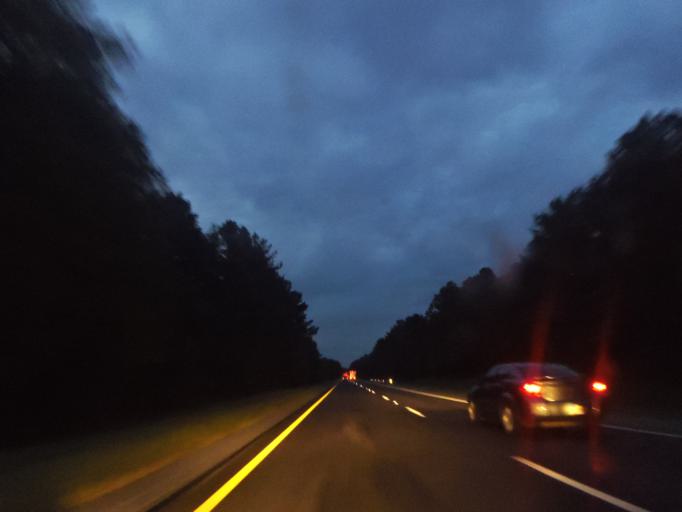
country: US
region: Alabama
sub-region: DeKalb County
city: Collinsville
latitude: 34.3029
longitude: -85.8585
